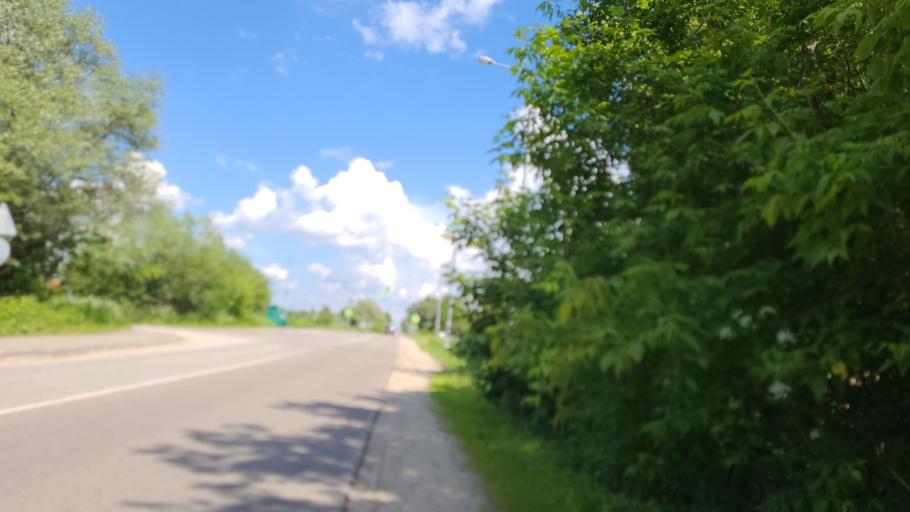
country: RU
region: Moskovskaya
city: Konobeyevo
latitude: 55.4015
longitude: 38.6655
